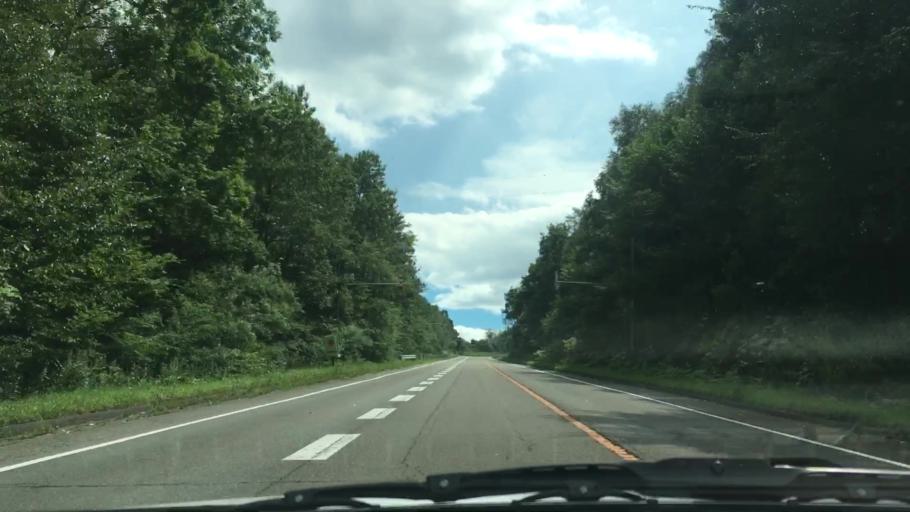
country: JP
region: Hokkaido
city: Otofuke
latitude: 43.2811
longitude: 143.4064
